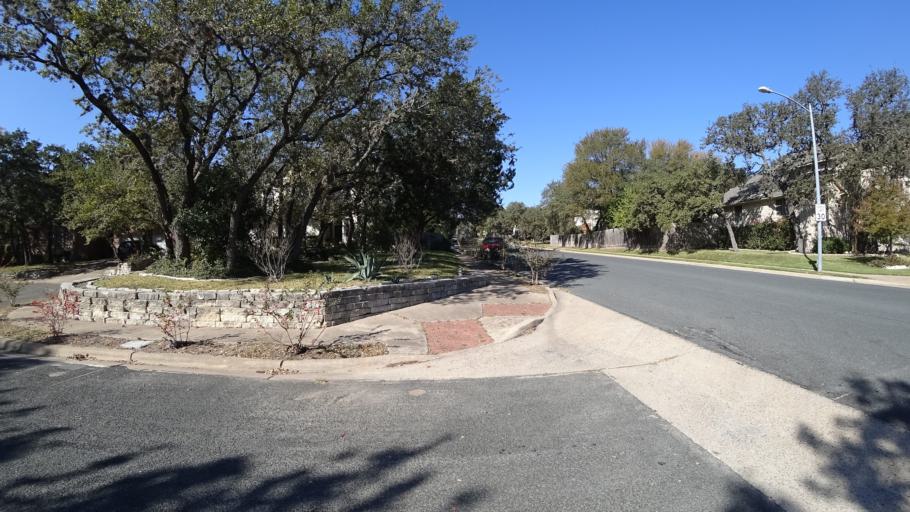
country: US
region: Texas
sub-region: Travis County
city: Barton Creek
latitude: 30.2277
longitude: -97.8684
